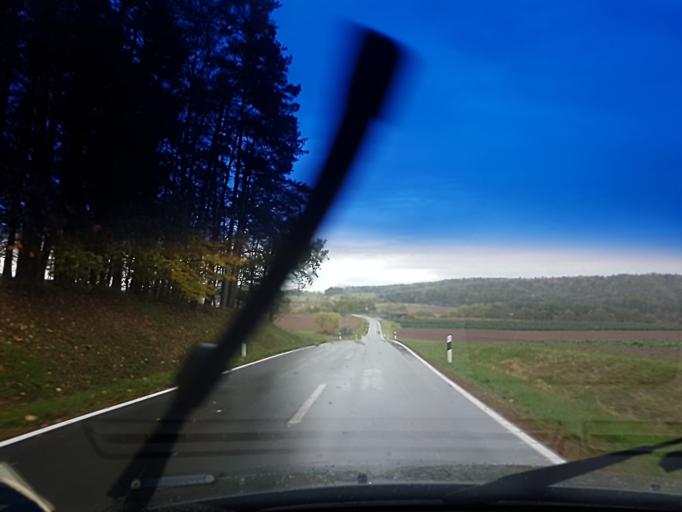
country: DE
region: Bavaria
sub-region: Upper Franconia
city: Schlusselfeld
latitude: 49.7601
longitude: 10.6659
